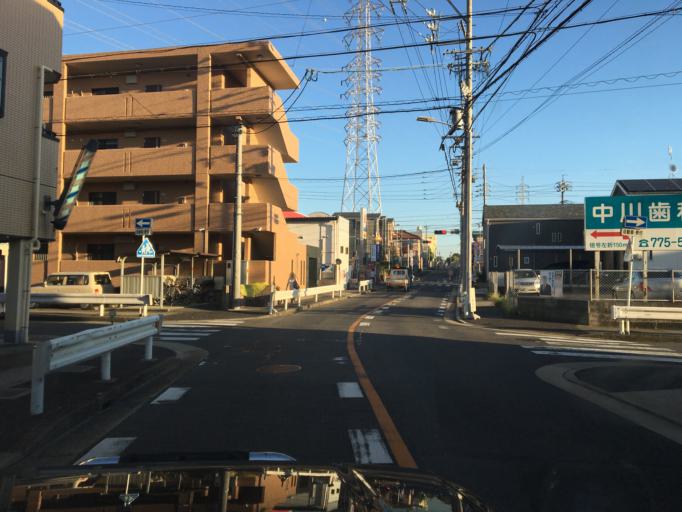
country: JP
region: Aichi
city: Kasugai
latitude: 35.1978
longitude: 137.0023
